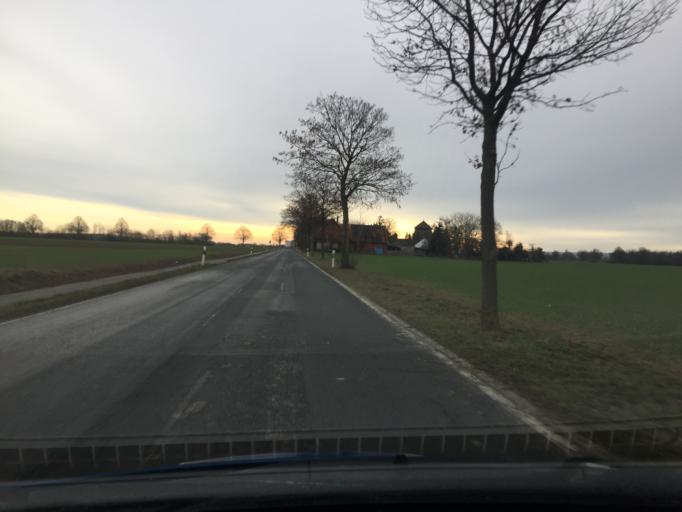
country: DE
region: Lower Saxony
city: Pattensen
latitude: 52.2828
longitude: 9.7662
